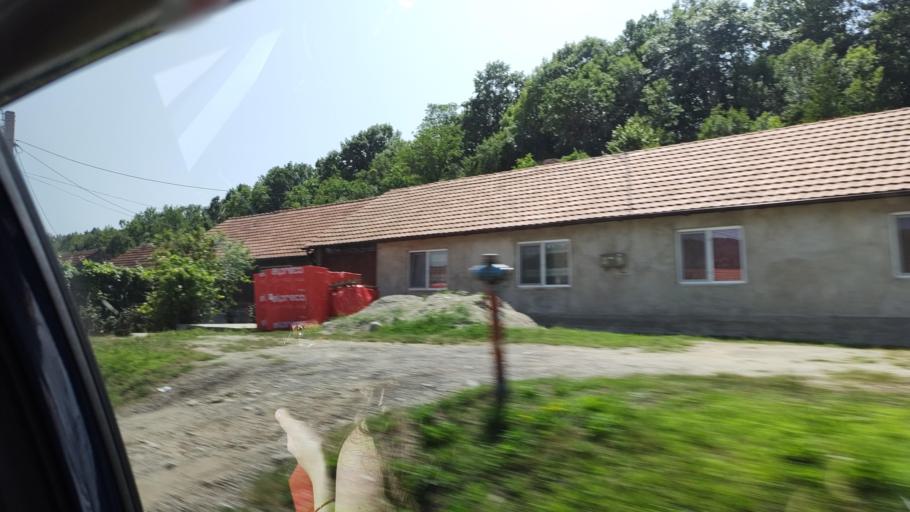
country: RO
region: Mehedinti
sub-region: Comuna Eselnita
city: Eselnita
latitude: 44.7102
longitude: 22.3592
